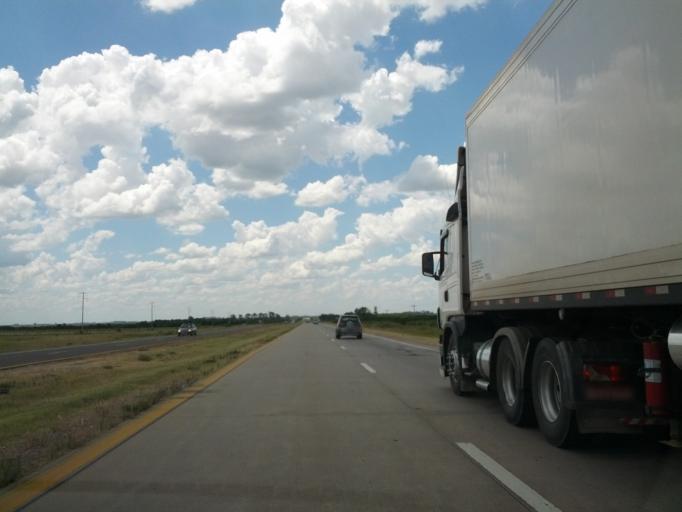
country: AR
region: Entre Rios
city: Gualeguaychu
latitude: -32.9945
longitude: -58.5996
